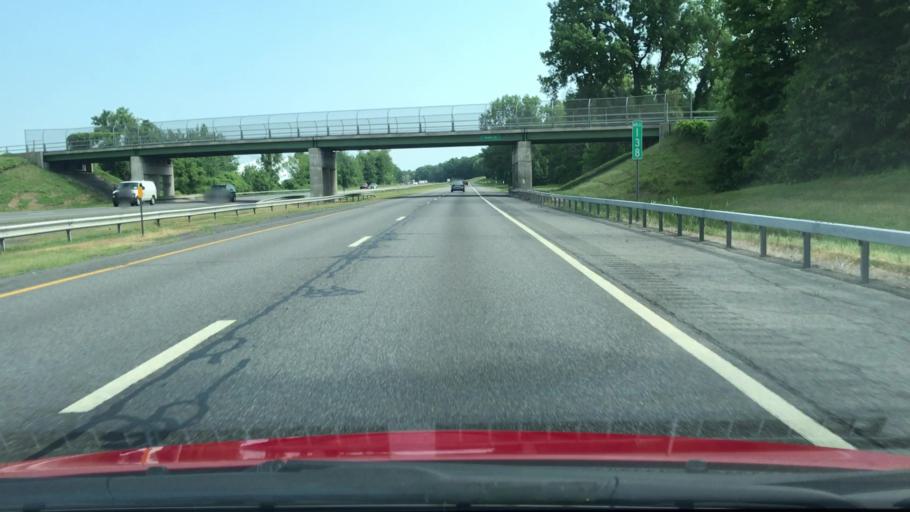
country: US
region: New York
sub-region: Albany County
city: Delmar
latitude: 42.5772
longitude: -73.7879
